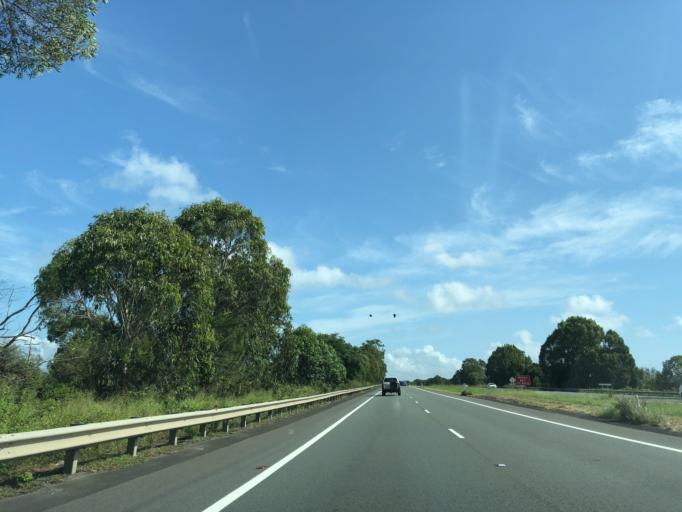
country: AU
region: New South Wales
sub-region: Byron Shire
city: Brunswick Heads
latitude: -28.6079
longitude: 153.5463
